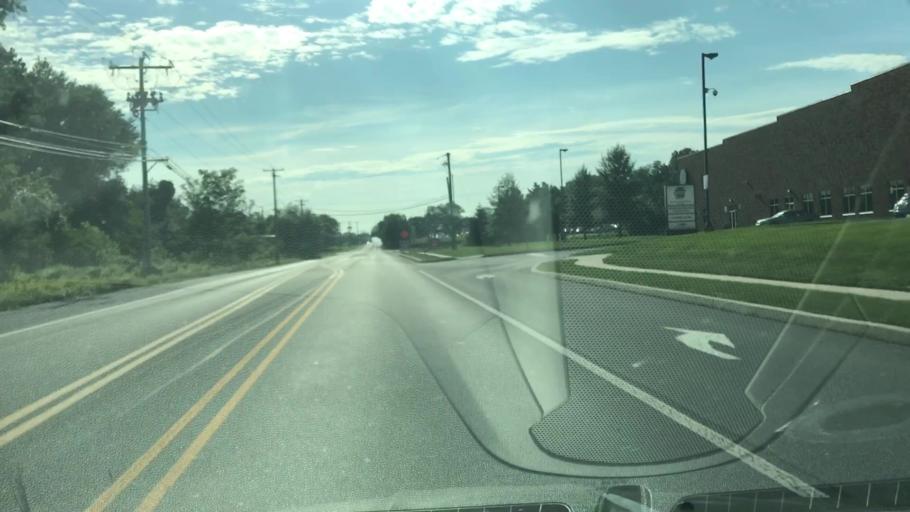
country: US
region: Pennsylvania
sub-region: Dauphin County
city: Highspire
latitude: 40.2277
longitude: -76.7604
